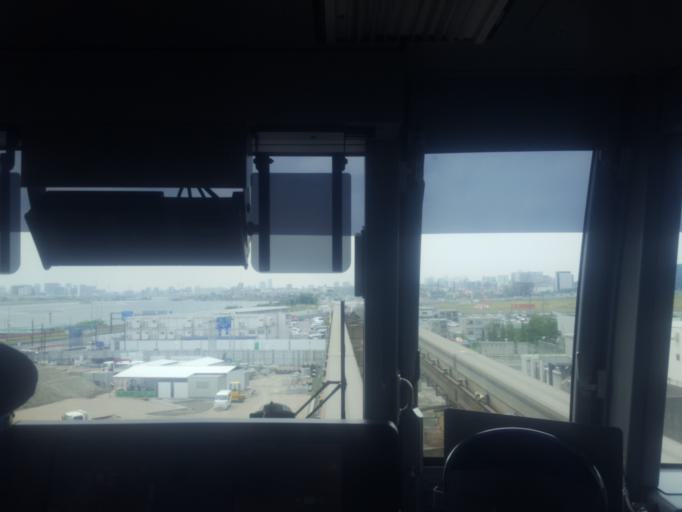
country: JP
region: Kanagawa
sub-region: Kawasaki-shi
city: Kawasaki
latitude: 35.5450
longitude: 139.7646
